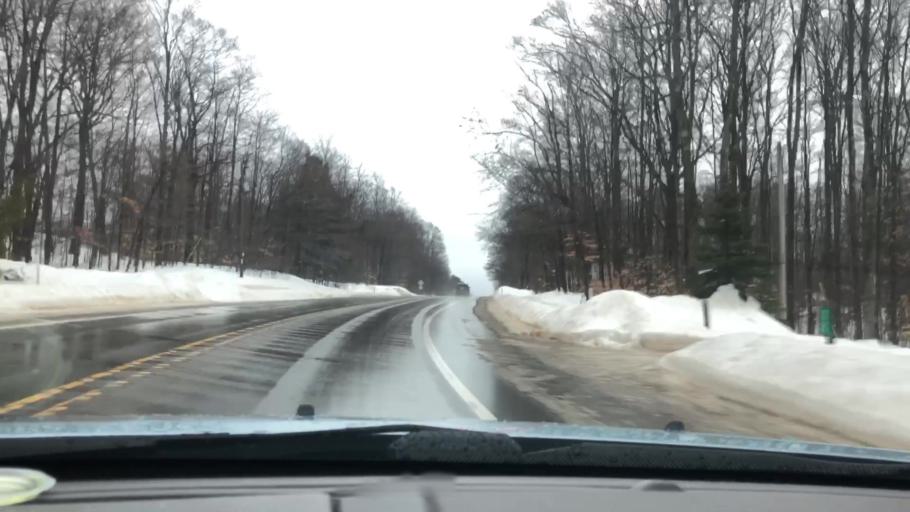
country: US
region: Michigan
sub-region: Charlevoix County
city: East Jordan
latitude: 45.1030
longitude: -85.0309
